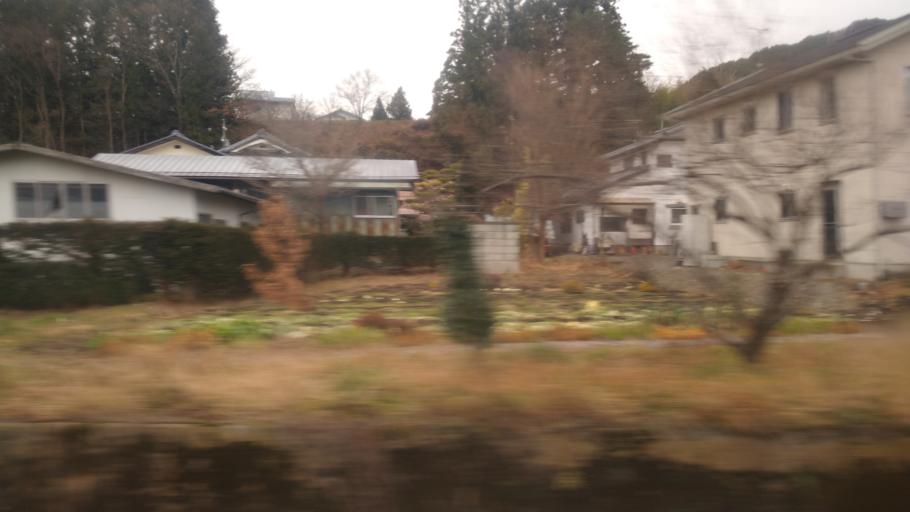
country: JP
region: Nagano
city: Shiojiri
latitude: 36.0819
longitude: 137.9119
